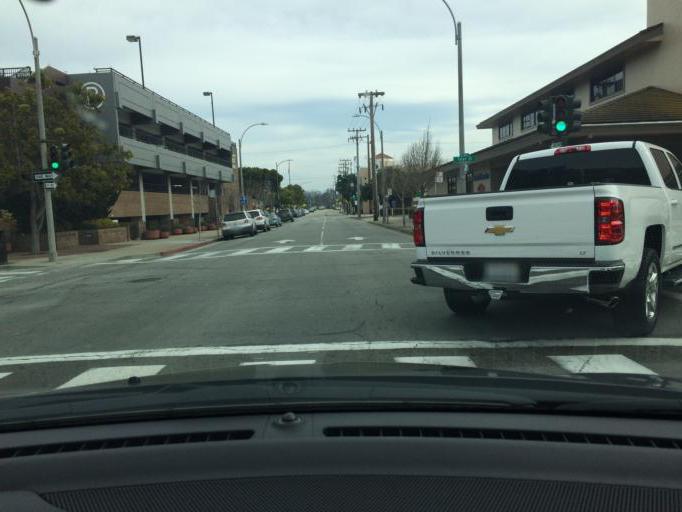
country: US
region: California
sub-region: Monterey County
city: Monterey
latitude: 36.5999
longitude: -121.8937
